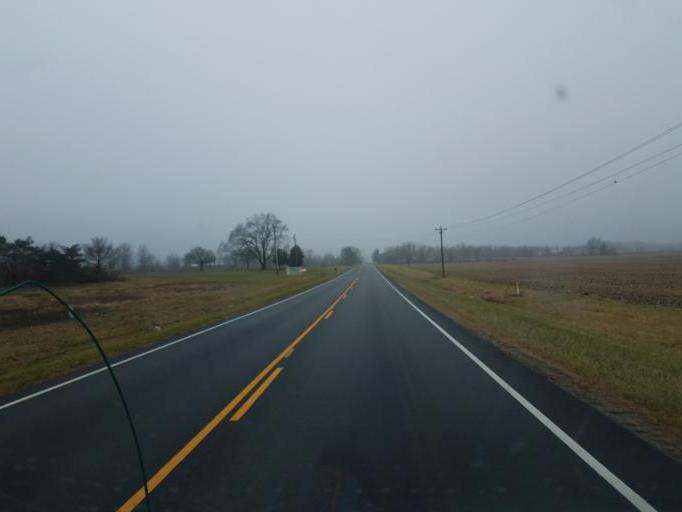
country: US
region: Ohio
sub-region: Union County
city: Marysville
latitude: 40.2497
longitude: -83.4210
